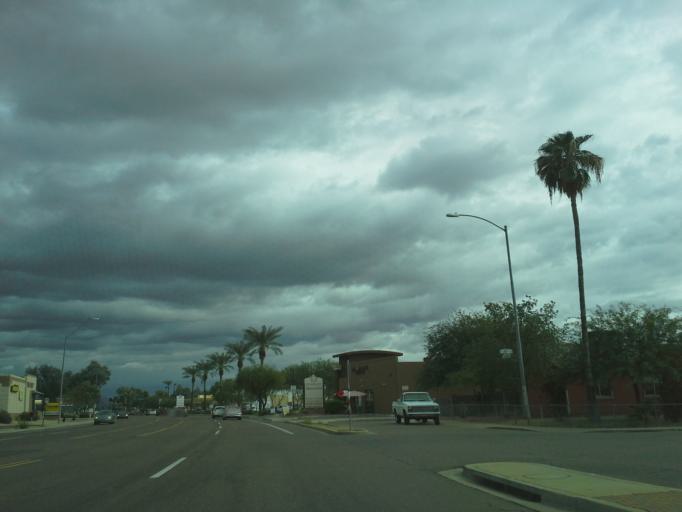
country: US
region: Arizona
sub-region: Maricopa County
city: Paradise Valley
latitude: 33.6120
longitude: -111.9994
